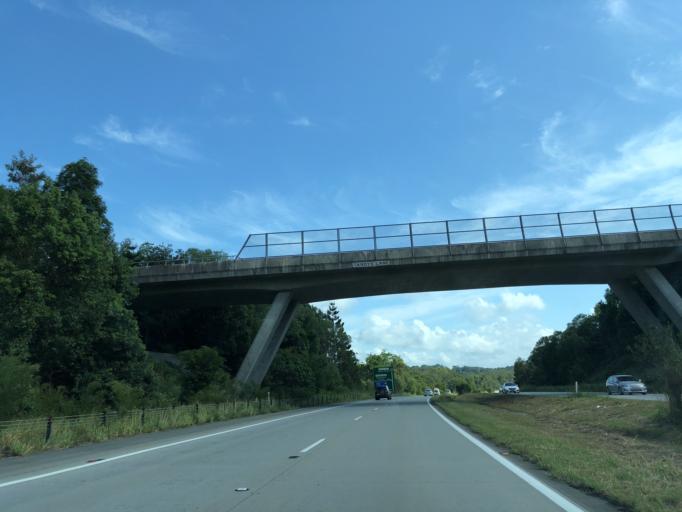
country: AU
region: New South Wales
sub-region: Byron Shire
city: Brunswick Heads
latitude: -28.5729
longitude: 153.5411
